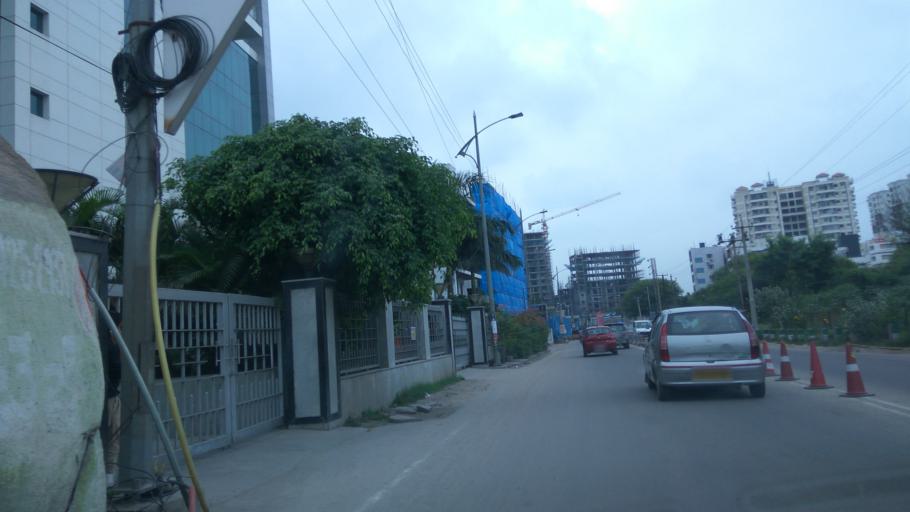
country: IN
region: Telangana
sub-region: Rangareddi
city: Kukatpalli
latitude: 17.4361
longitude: 78.3884
